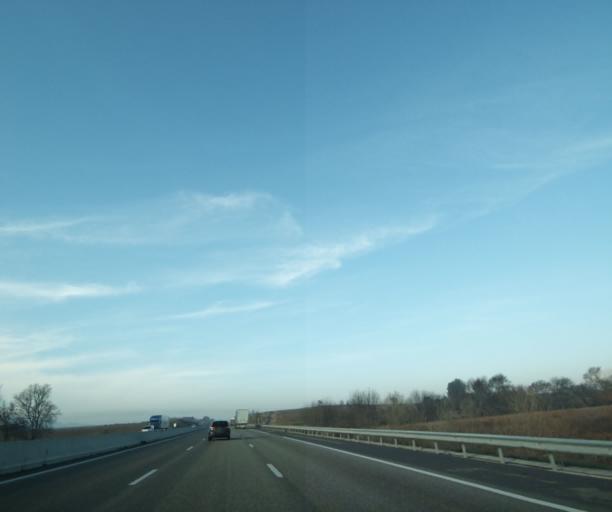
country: FR
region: Provence-Alpes-Cote d'Azur
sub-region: Departement des Bouches-du-Rhone
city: Trets
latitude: 43.4706
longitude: 5.6673
